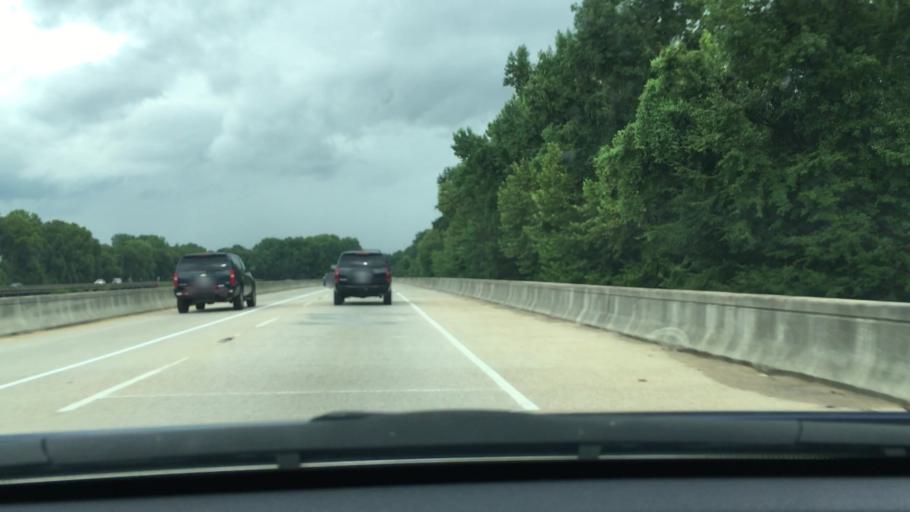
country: US
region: South Carolina
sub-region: Sumter County
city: Stateburg
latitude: 33.9470
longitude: -80.6273
